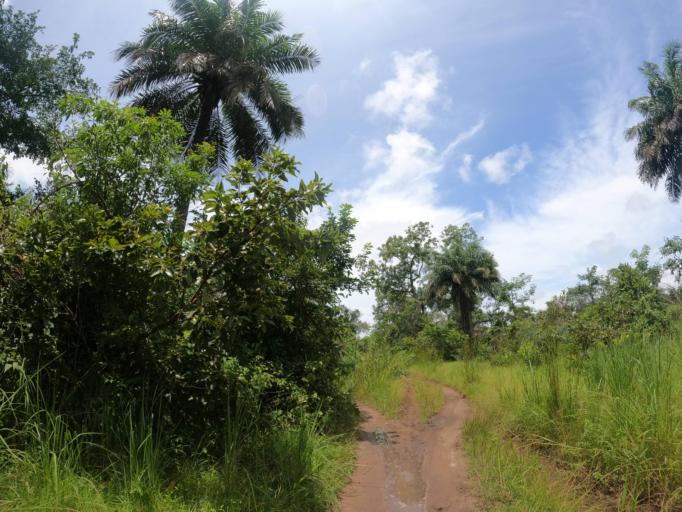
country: SL
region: Northern Province
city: Binkolo
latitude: 9.1441
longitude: -12.2431
